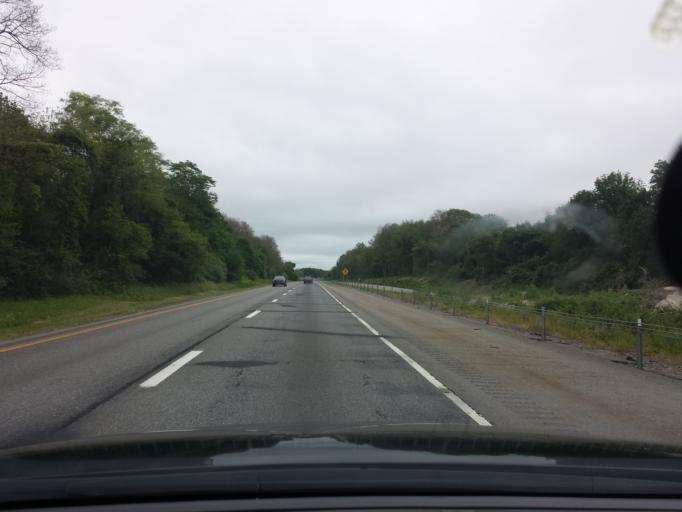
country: US
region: Connecticut
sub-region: New London County
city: Old Mystic
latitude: 41.3790
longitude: -71.9036
